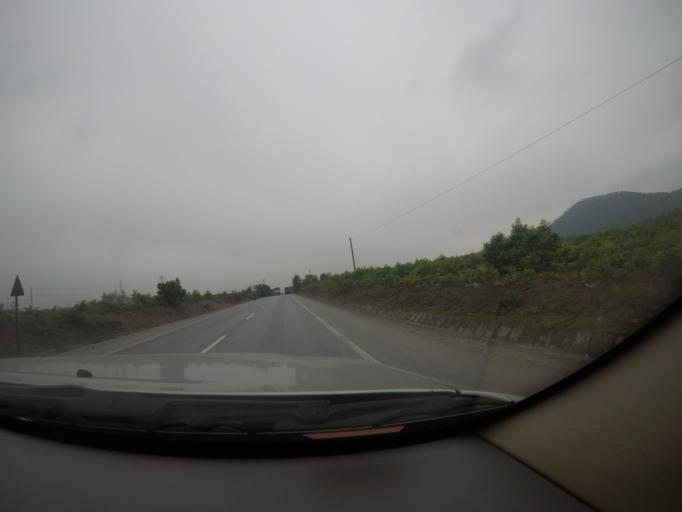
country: VN
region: Ha Tinh
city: Ky Anh
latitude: 18.0280
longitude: 106.3345
